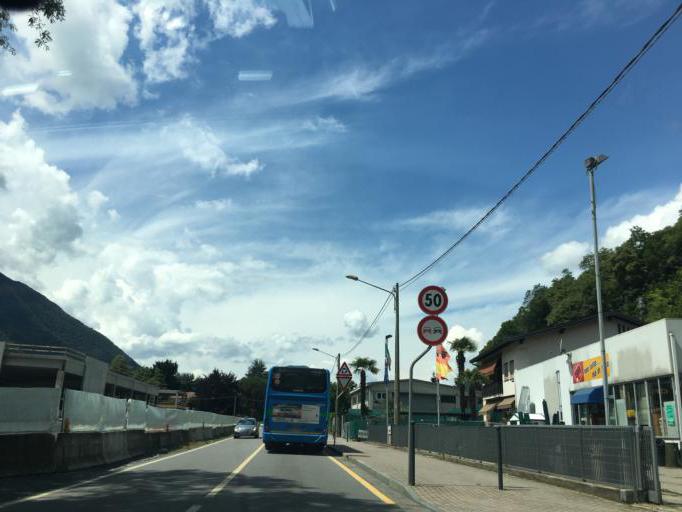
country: IT
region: Lombardy
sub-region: Provincia di Como
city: Carlazzo
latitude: 46.0426
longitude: 9.1520
